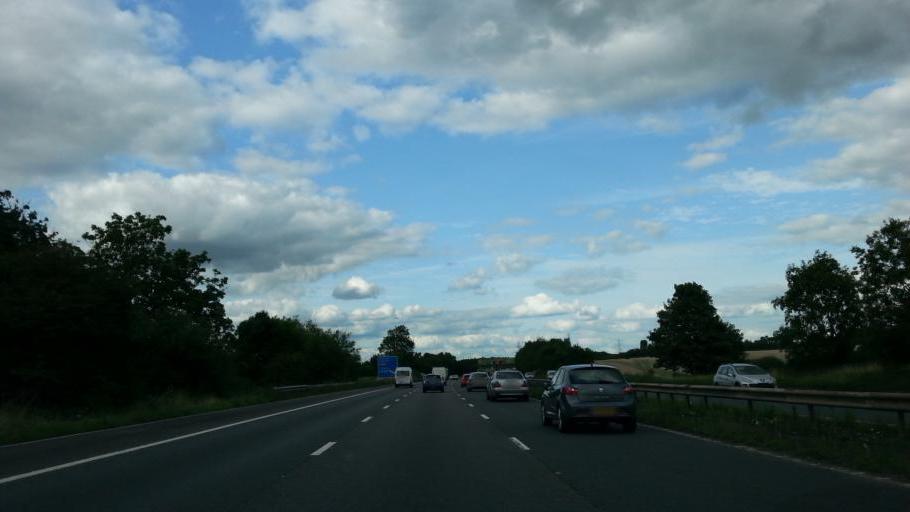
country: GB
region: England
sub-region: Leicestershire
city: Hinckley
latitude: 52.5008
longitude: -1.3824
